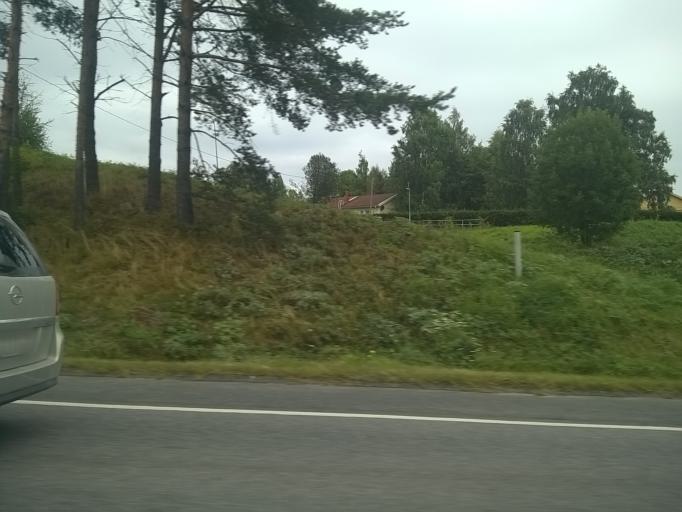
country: FI
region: Pirkanmaa
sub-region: Tampere
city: Tampere
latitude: 61.4785
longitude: 23.8324
